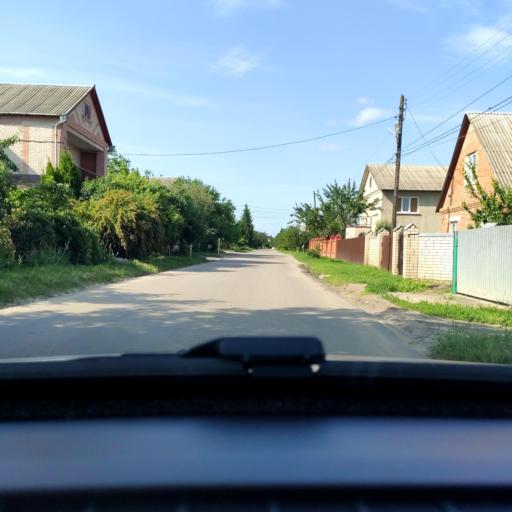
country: RU
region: Voronezj
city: Semiluki
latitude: 51.7068
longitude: 39.0291
